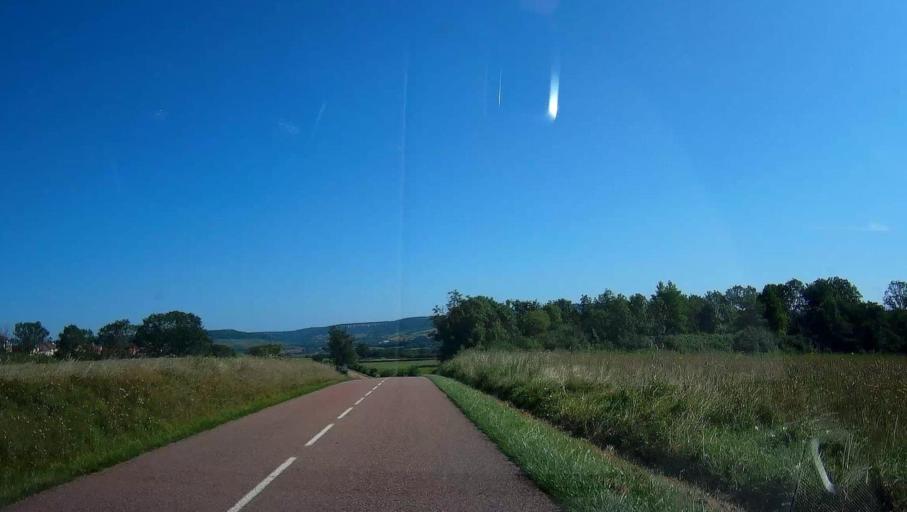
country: FR
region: Bourgogne
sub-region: Departement de la Cote-d'Or
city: Nolay
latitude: 46.9246
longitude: 4.6222
